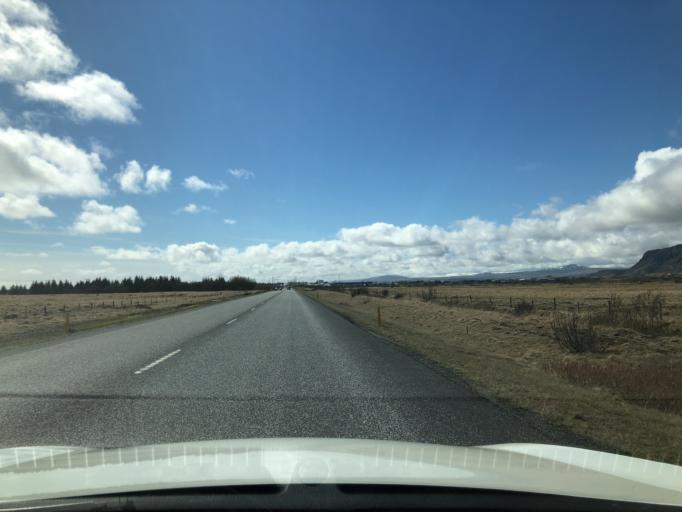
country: IS
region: South
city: Selfoss
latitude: 63.9405
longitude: -20.9510
